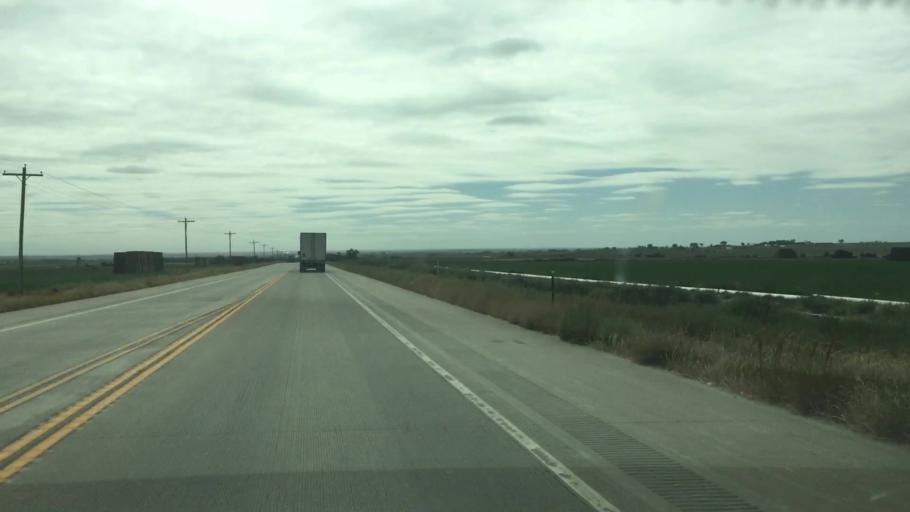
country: US
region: Colorado
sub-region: Prowers County
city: Lamar
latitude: 38.1966
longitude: -102.7242
